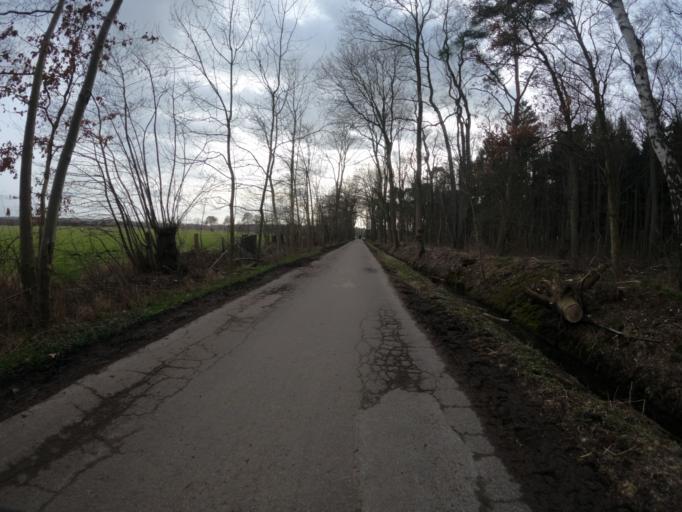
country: DE
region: Schleswig-Holstein
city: Rellingen
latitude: 53.6066
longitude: 9.7834
